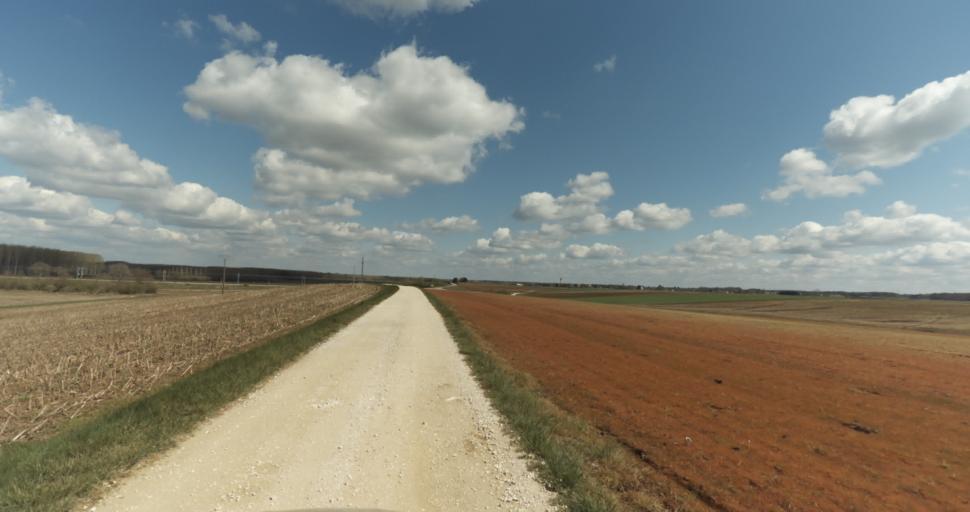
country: FR
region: Bourgogne
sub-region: Departement de la Cote-d'Or
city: Auxonne
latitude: 47.2197
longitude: 5.4221
